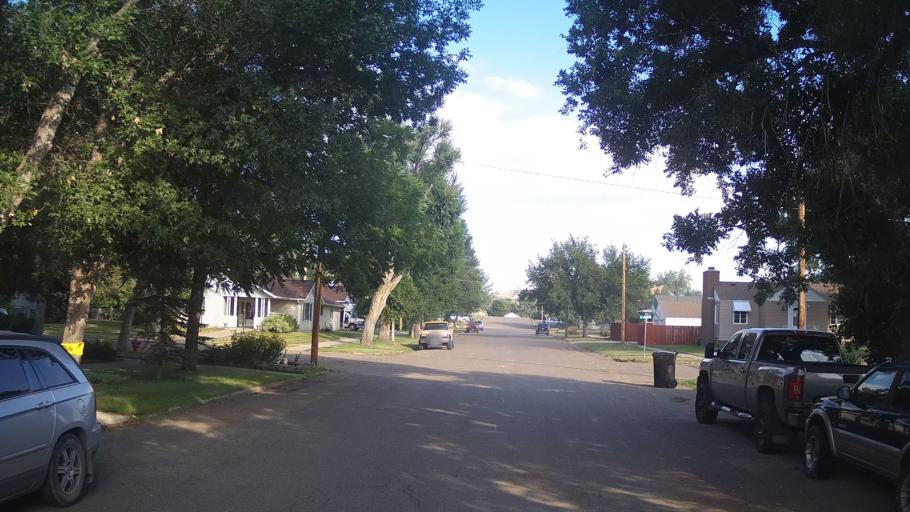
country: US
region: Montana
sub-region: Dawson County
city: Glendive
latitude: 47.0974
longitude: -104.7137
